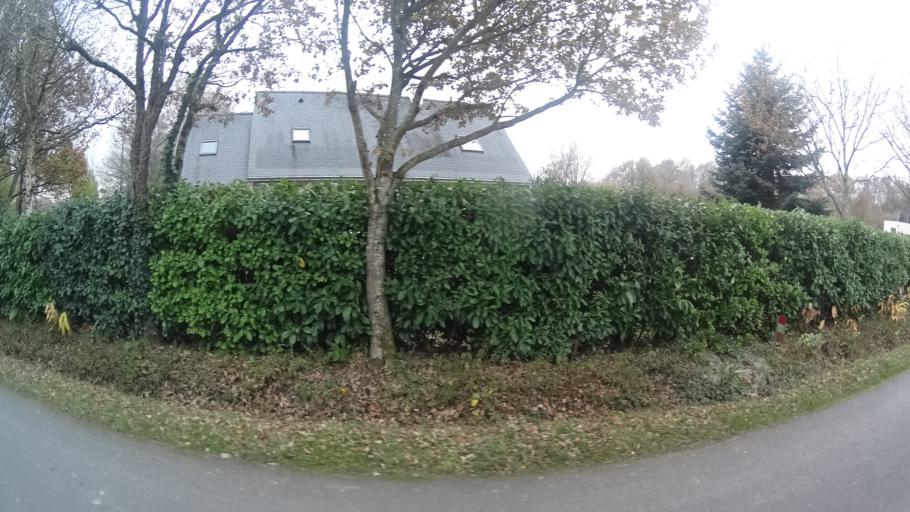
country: FR
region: Brittany
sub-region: Departement d'Ille-et-Vilaine
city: Langon
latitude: 47.6679
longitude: -1.9103
